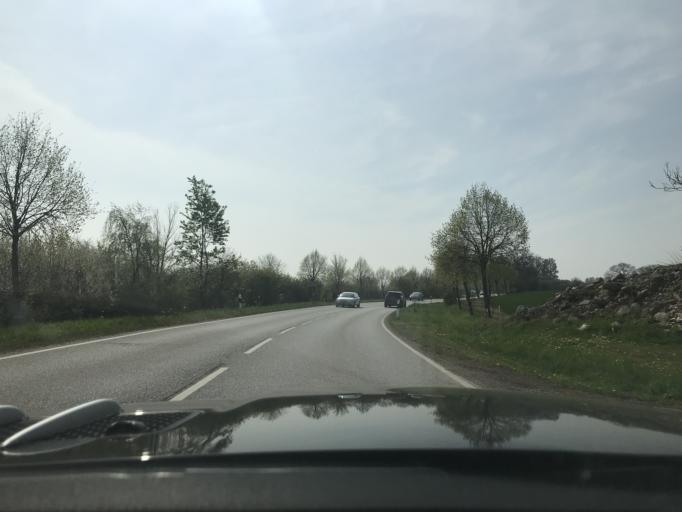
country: DE
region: Schleswig-Holstein
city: Gromitz
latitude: 54.1763
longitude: 10.9763
